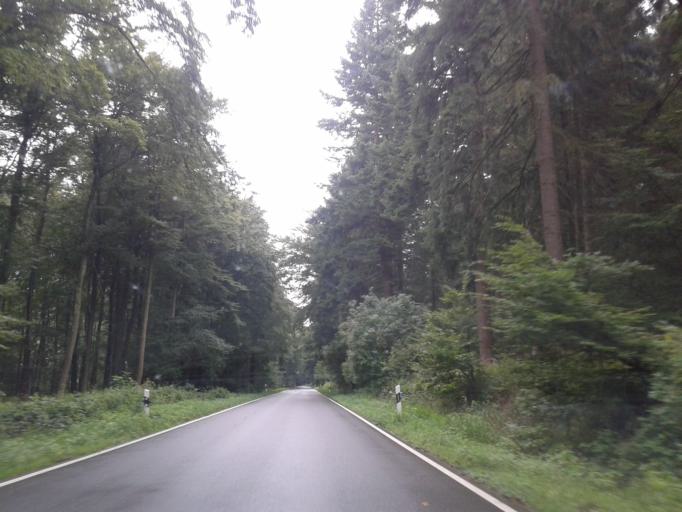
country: DE
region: North Rhine-Westphalia
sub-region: Regierungsbezirk Detmold
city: Barntrup
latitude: 51.9666
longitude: 9.1449
